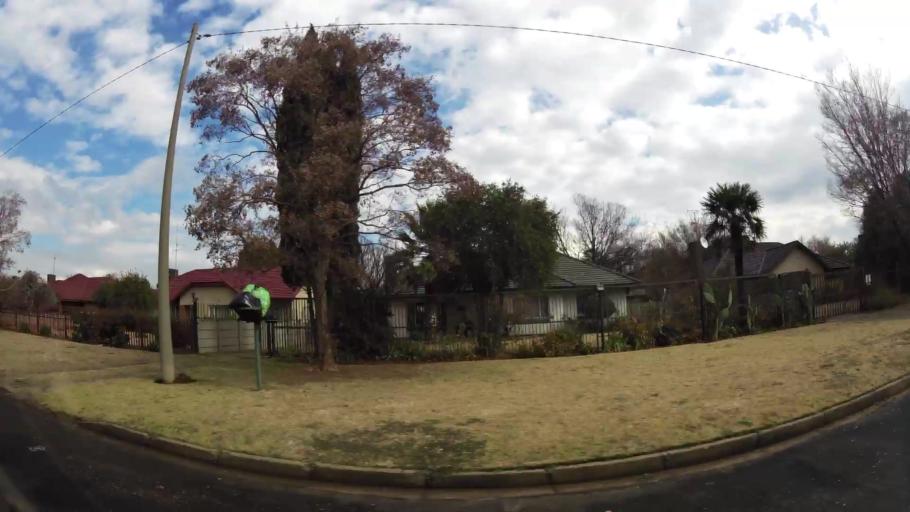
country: ZA
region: Gauteng
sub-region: Sedibeng District Municipality
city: Vereeniging
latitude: -26.6547
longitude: 27.9927
